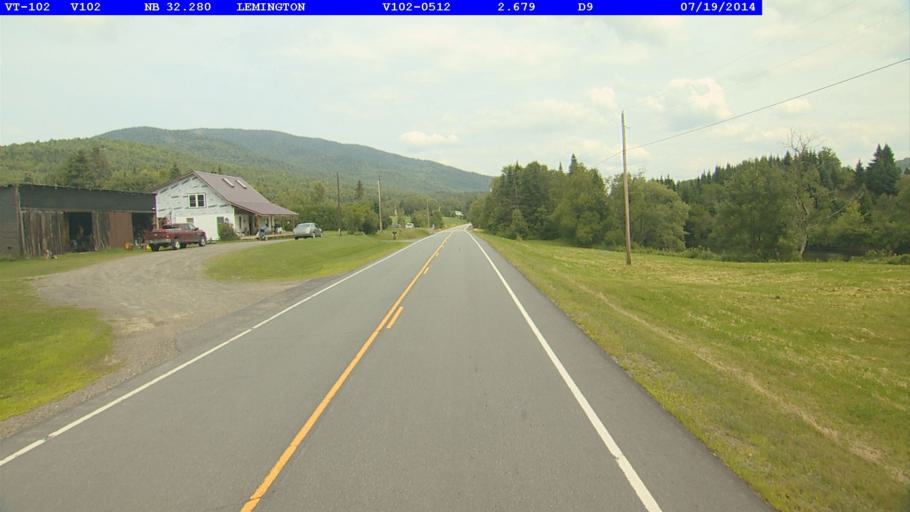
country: US
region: New Hampshire
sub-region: Coos County
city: Colebrook
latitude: 44.8606
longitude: -71.5514
